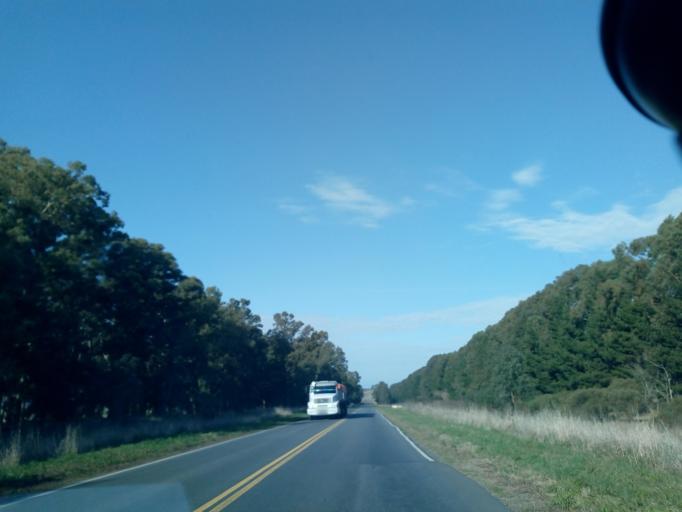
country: AR
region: Buenos Aires
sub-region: Partido de Tandil
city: Tandil
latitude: -37.3542
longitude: -58.8796
